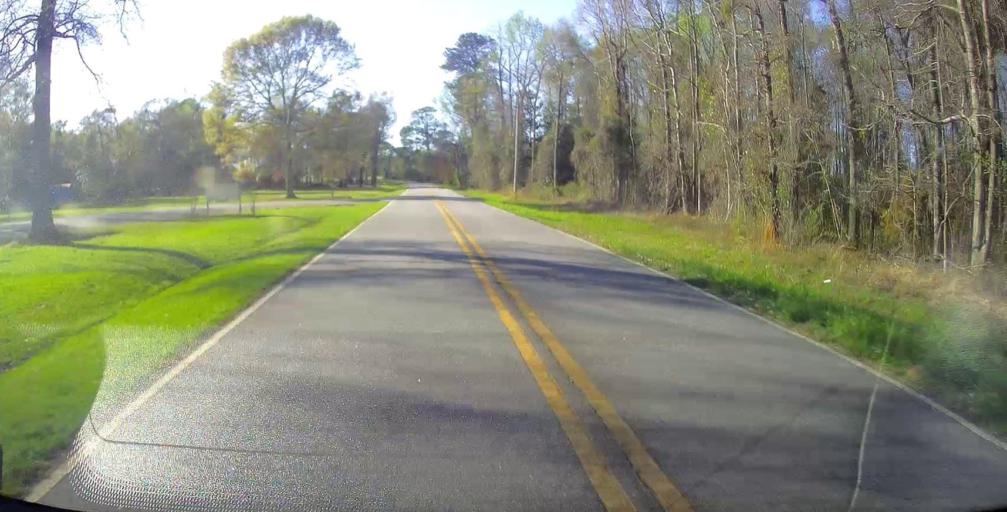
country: US
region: Georgia
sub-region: Houston County
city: Perry
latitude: 32.3624
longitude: -83.6547
